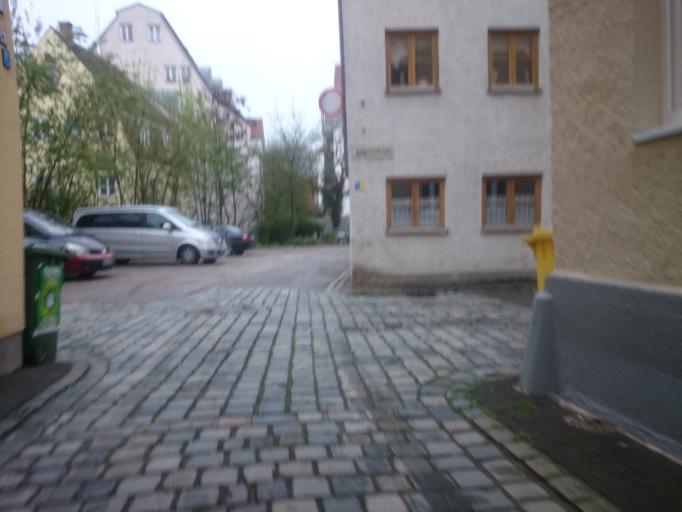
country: DE
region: Bavaria
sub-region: Swabia
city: Augsburg
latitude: 48.3714
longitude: 10.9026
